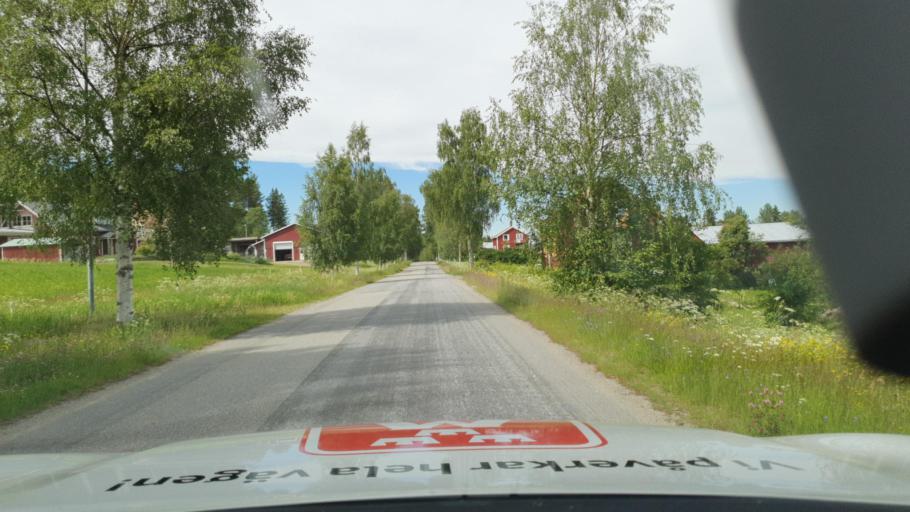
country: SE
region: Vaesterbotten
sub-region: Skelleftea Kommun
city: Burtraesk
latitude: 64.4267
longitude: 20.5300
